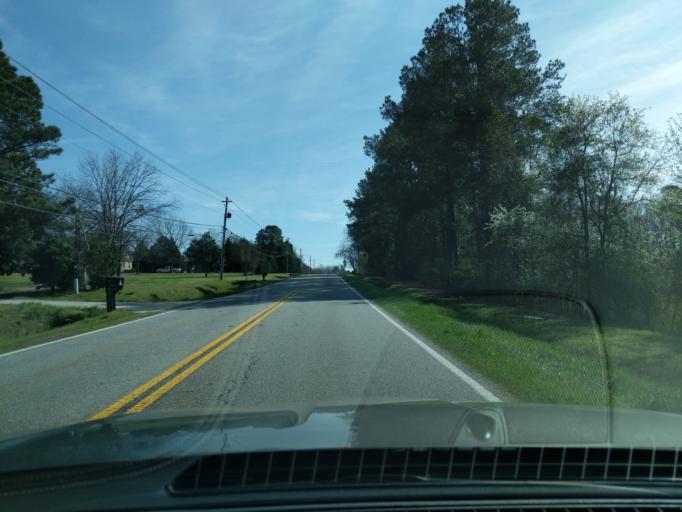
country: US
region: Georgia
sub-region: Columbia County
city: Evans
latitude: 33.5303
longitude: -82.1637
